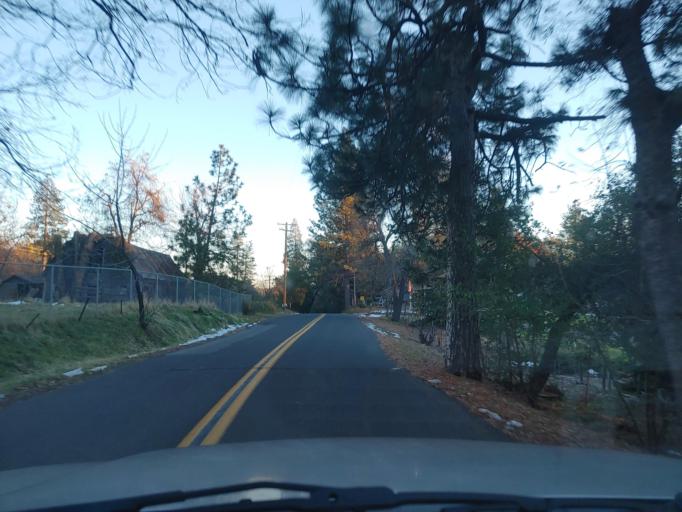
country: US
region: California
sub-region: Tuolumne County
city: Cedar Ridge
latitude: 38.0378
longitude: -120.2760
